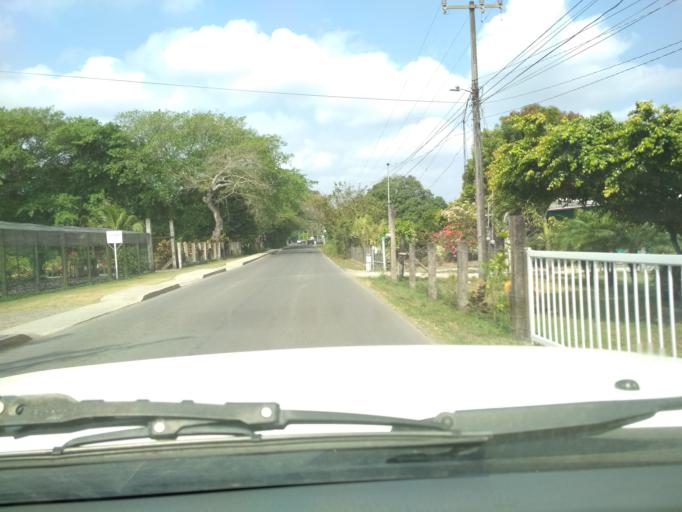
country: MX
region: Veracruz
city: El Tejar
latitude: 19.0766
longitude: -96.1680
